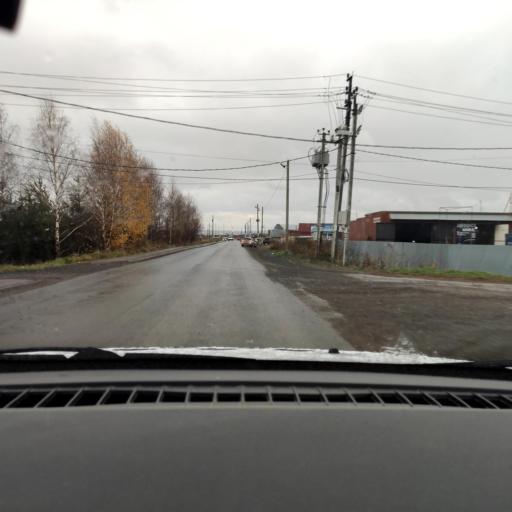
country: RU
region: Perm
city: Kultayevo
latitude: 57.8992
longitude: 55.9611
